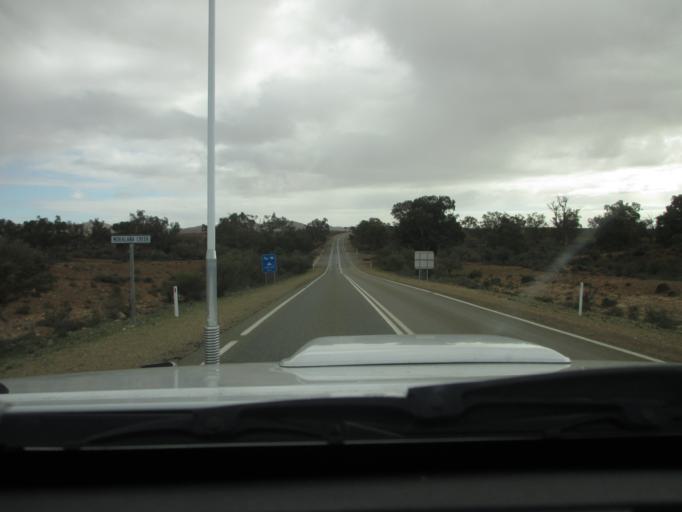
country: AU
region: South Australia
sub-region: Flinders Ranges
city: Quorn
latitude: -31.5507
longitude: 138.4258
